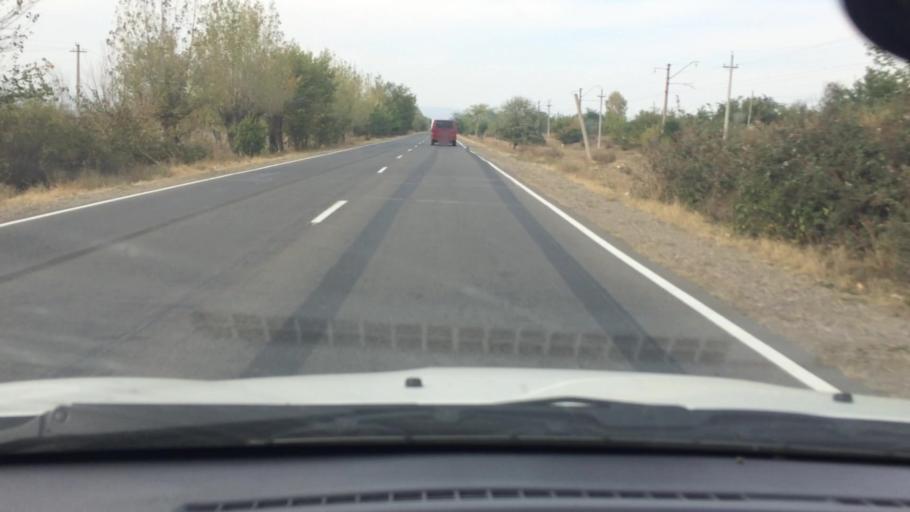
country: GE
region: Kvemo Kartli
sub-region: Marneuli
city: Marneuli
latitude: 41.4430
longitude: 44.8166
